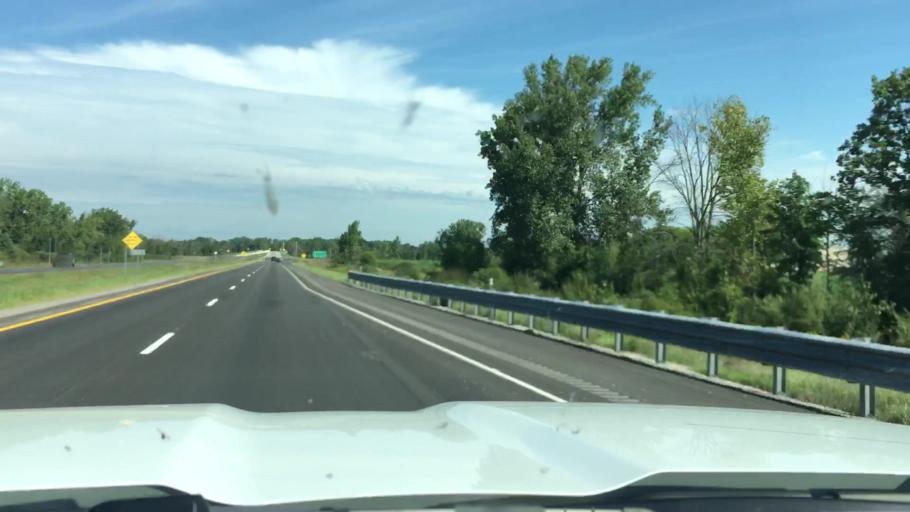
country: US
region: Michigan
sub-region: Saginaw County
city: Freeland
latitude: 43.5897
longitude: -84.1393
